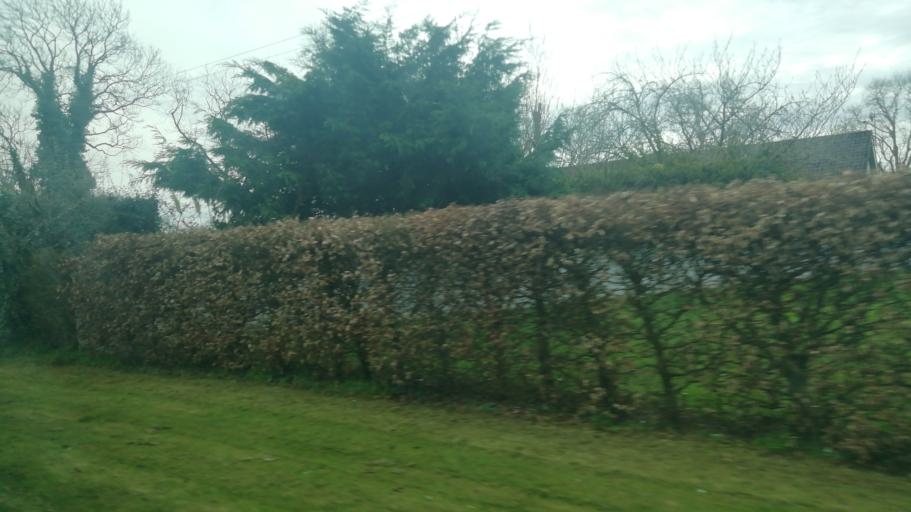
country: IE
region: Leinster
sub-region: Kildare
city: Derrinturn
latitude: 53.3323
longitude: -6.9283
